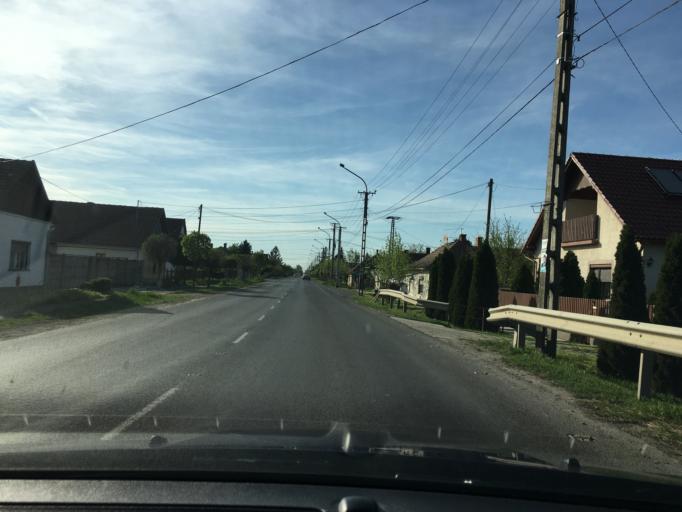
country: HU
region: Bekes
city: Korostarcsa
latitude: 46.8713
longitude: 21.0266
